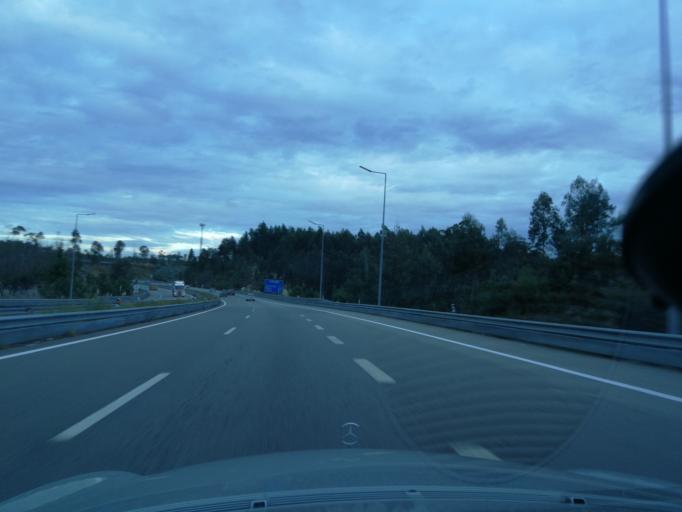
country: PT
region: Aveiro
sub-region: Estarreja
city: Salreu
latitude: 40.6921
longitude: -8.5373
